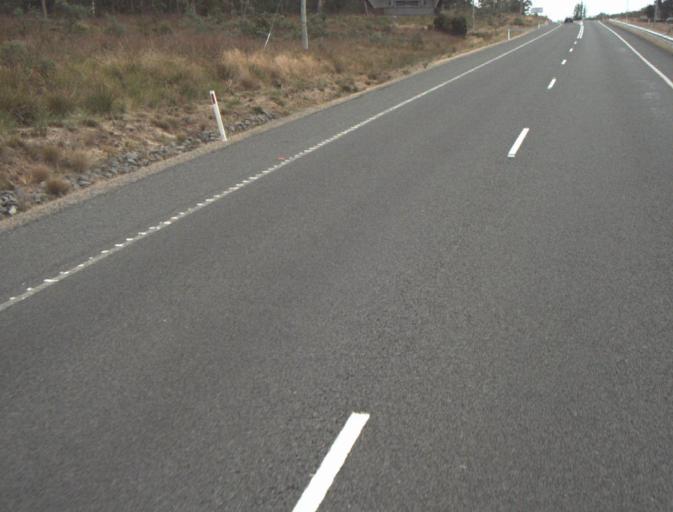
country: AU
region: Tasmania
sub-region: Launceston
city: Mayfield
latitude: -41.2698
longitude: 147.0346
